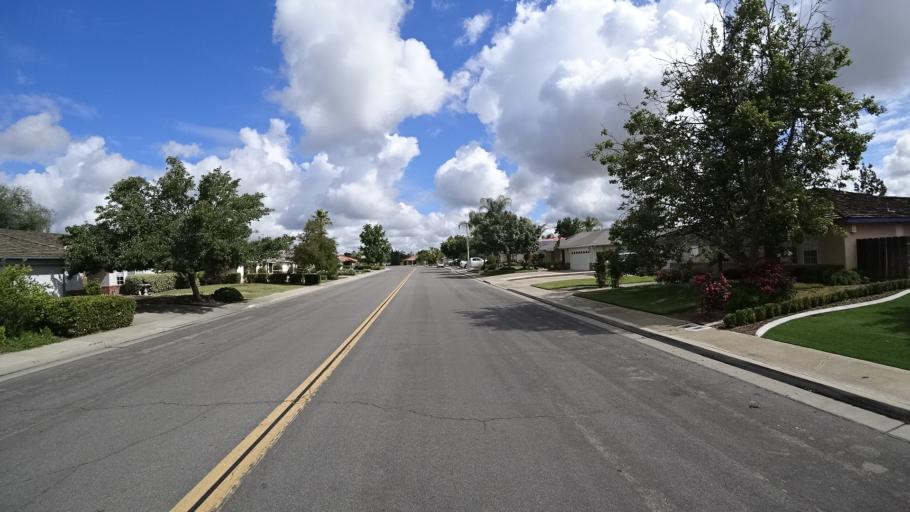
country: US
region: California
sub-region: Kings County
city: Lucerne
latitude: 36.3645
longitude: -119.6491
